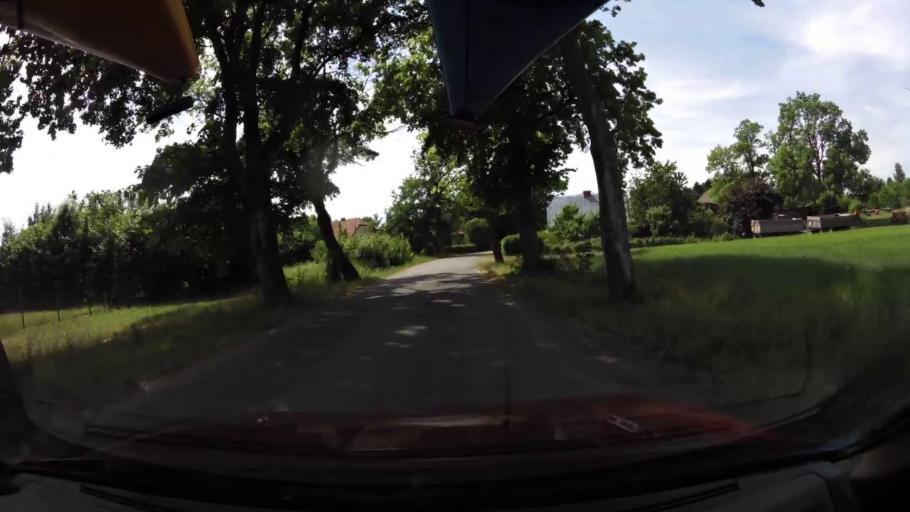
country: PL
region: West Pomeranian Voivodeship
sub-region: Powiat slawienski
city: Darlowo
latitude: 54.3088
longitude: 16.4805
